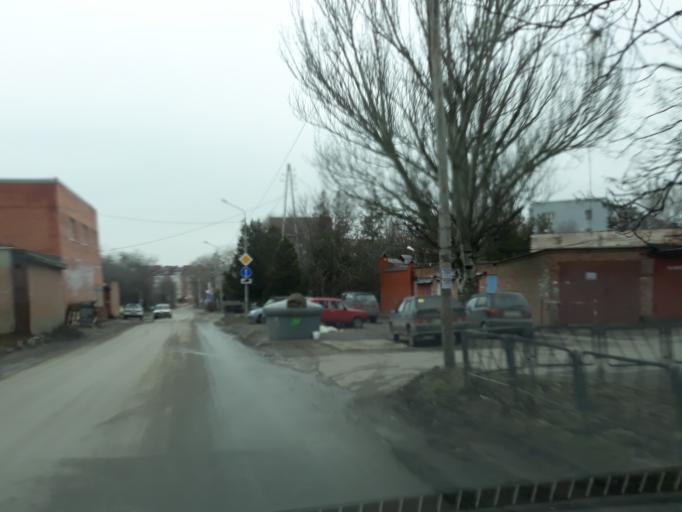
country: RU
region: Rostov
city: Taganrog
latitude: 47.2066
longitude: 38.8976
